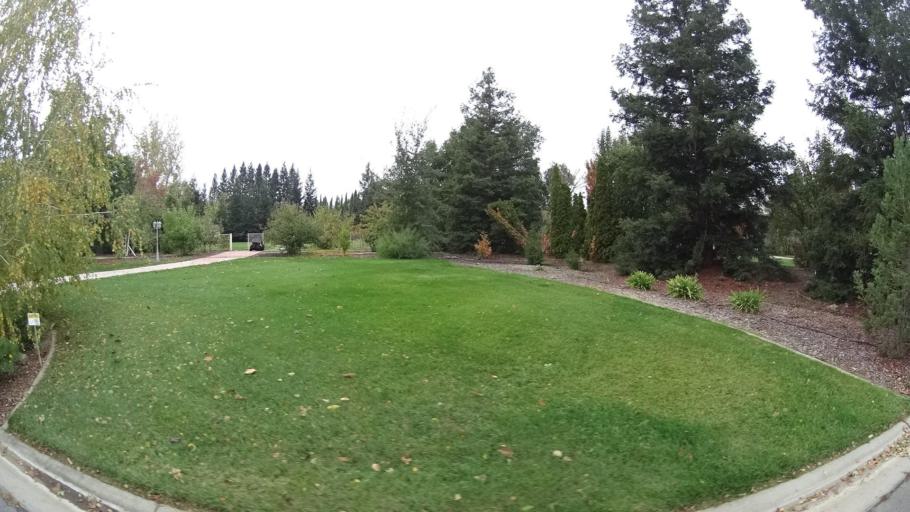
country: US
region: California
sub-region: Sacramento County
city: Wilton
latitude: 38.4442
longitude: -121.2949
